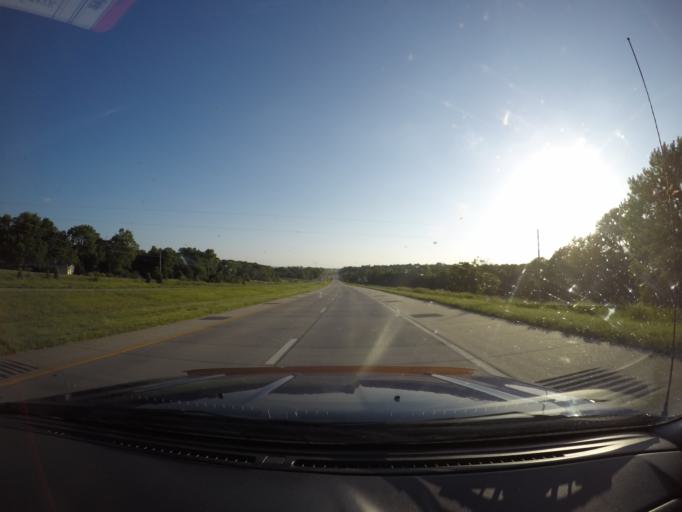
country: US
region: Kansas
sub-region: Pottawatomie County
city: Wamego
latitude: 39.2084
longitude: -96.4177
